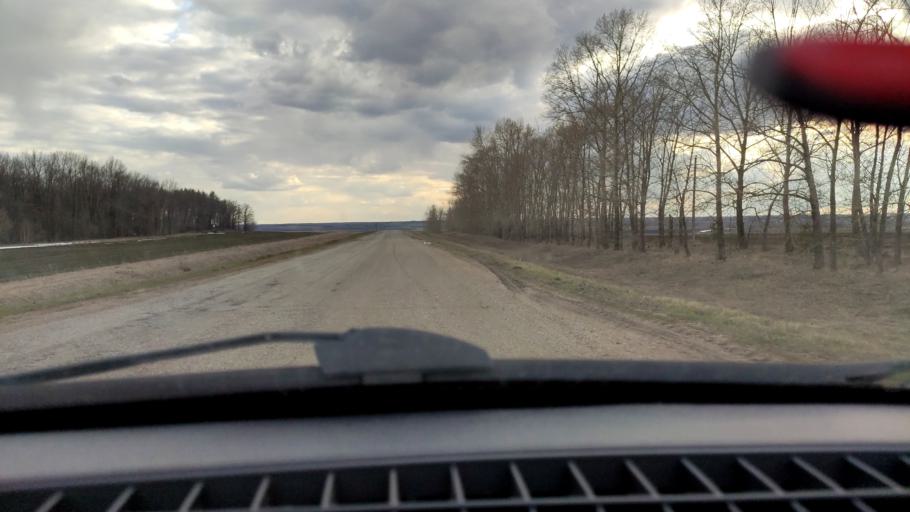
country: RU
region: Bashkortostan
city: Karmaskaly
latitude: 54.3013
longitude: 55.9271
